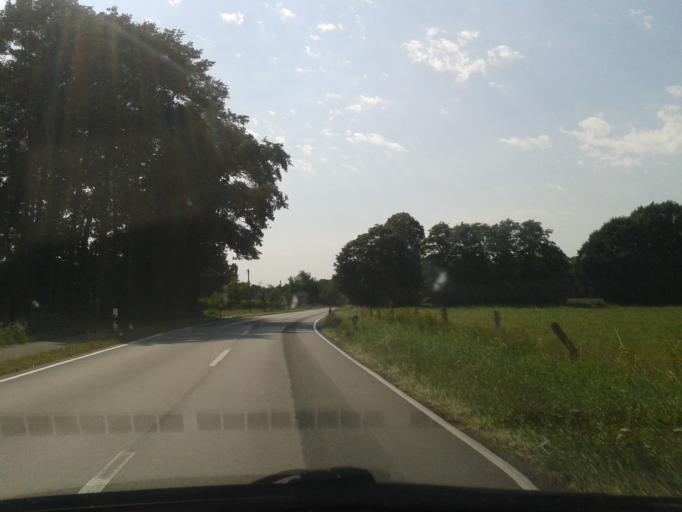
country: DE
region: North Rhine-Westphalia
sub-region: Regierungsbezirk Detmold
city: Hovelhof
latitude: 51.8665
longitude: 8.5935
